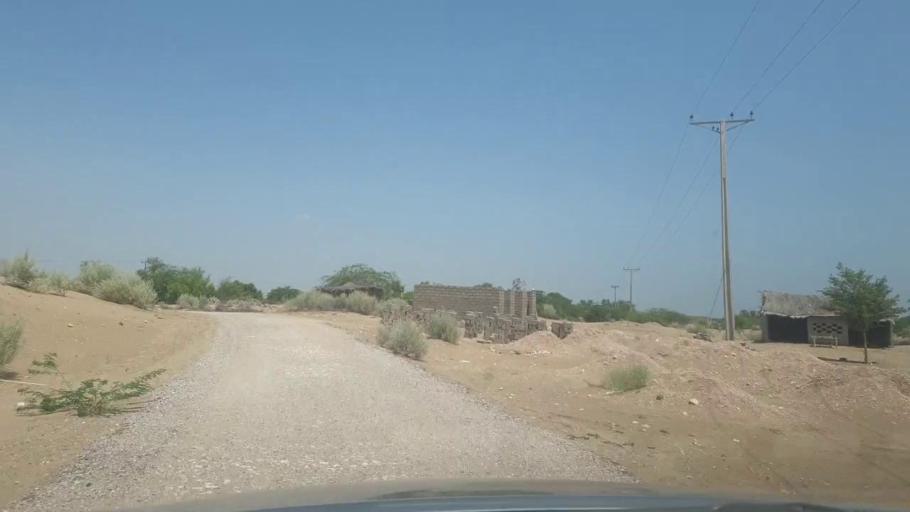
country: PK
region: Sindh
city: Kot Diji
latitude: 27.3294
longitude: 69.0113
